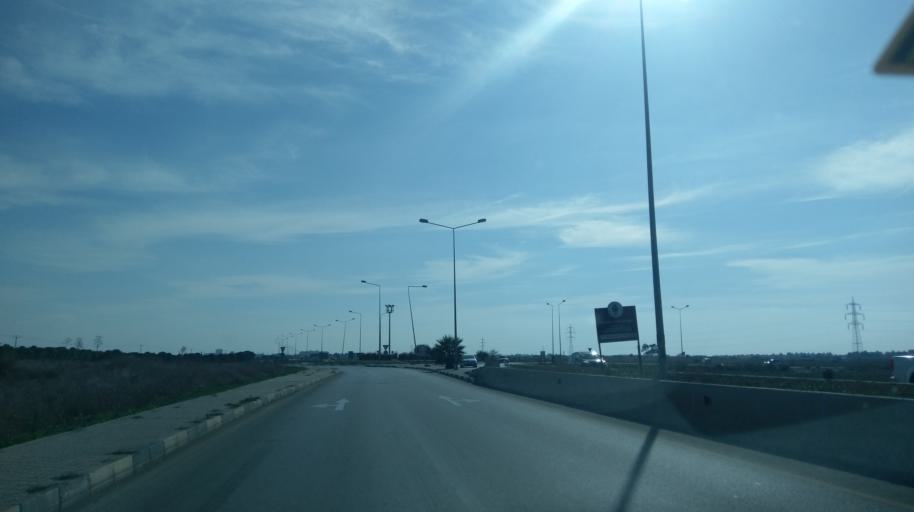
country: CY
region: Ammochostos
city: Famagusta
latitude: 35.1796
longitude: 33.8958
